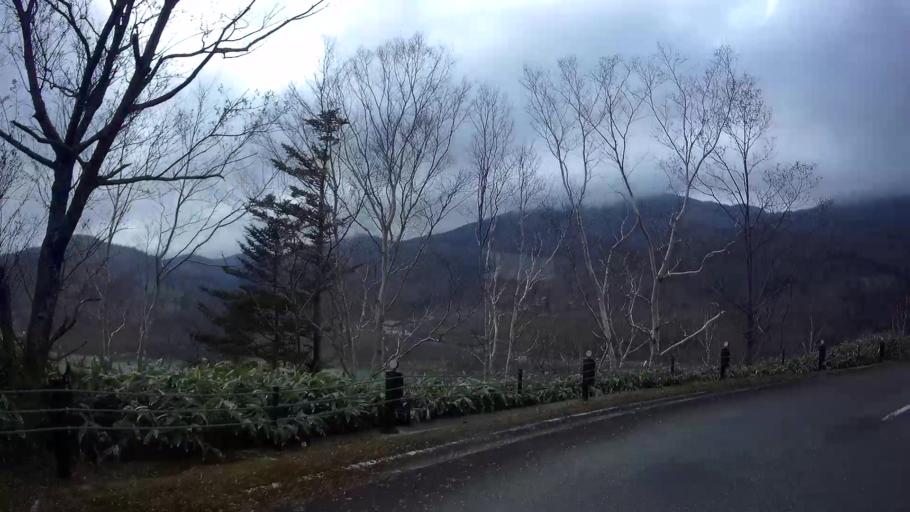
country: JP
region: Gunma
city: Nakanojomachi
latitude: 36.7180
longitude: 138.6449
